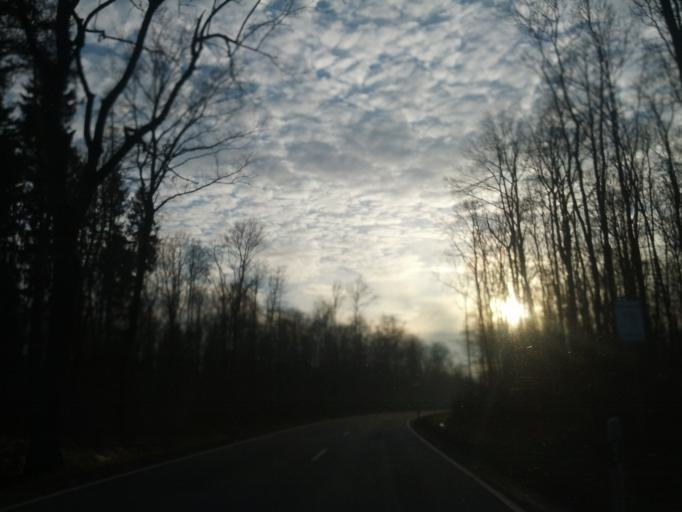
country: DE
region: Thuringia
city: Wangenheim
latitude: 51.0582
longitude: 10.5772
